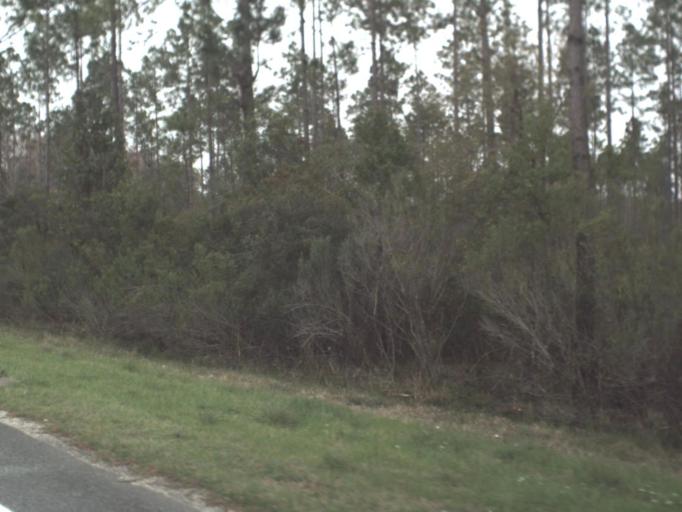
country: US
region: Florida
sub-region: Leon County
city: Woodville
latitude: 30.1953
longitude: -84.1407
